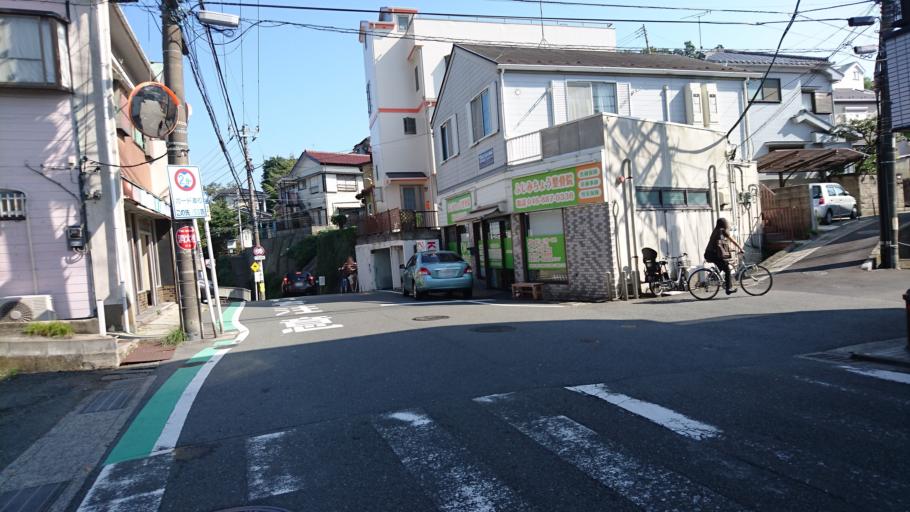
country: JP
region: Kanagawa
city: Yokosuka
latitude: 35.2685
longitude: 139.6762
